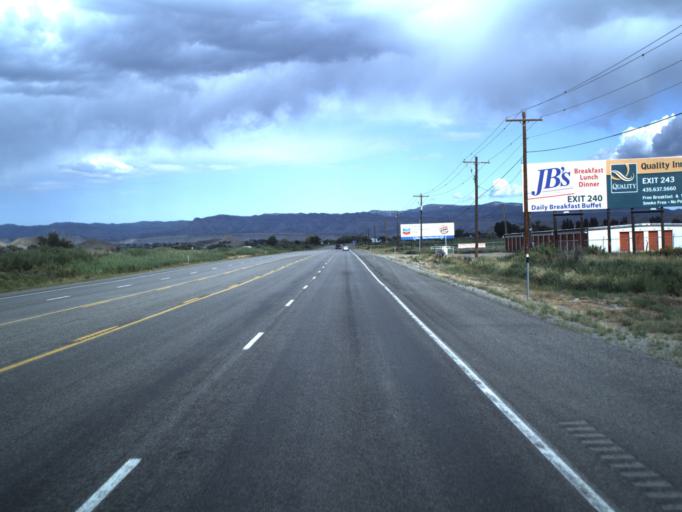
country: US
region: Utah
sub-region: Carbon County
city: Wellington
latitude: 39.5630
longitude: -110.7702
